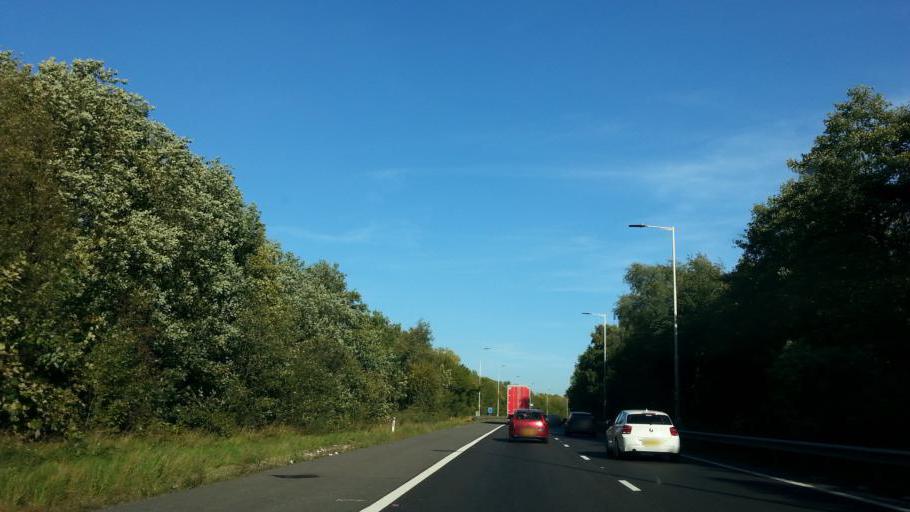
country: GB
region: England
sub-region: Staffordshire
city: Essington
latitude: 52.6371
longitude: -2.0629
